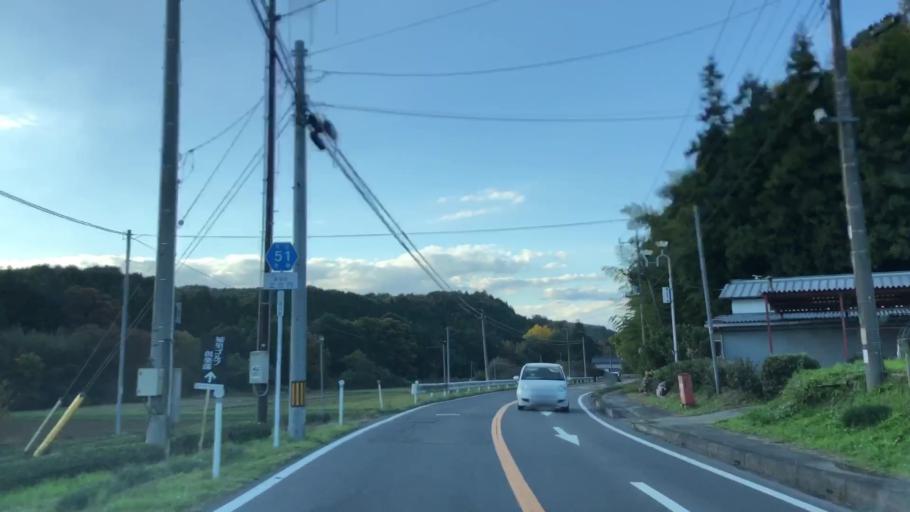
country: JP
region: Ibaraki
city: Kasama
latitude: 36.4620
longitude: 140.3231
